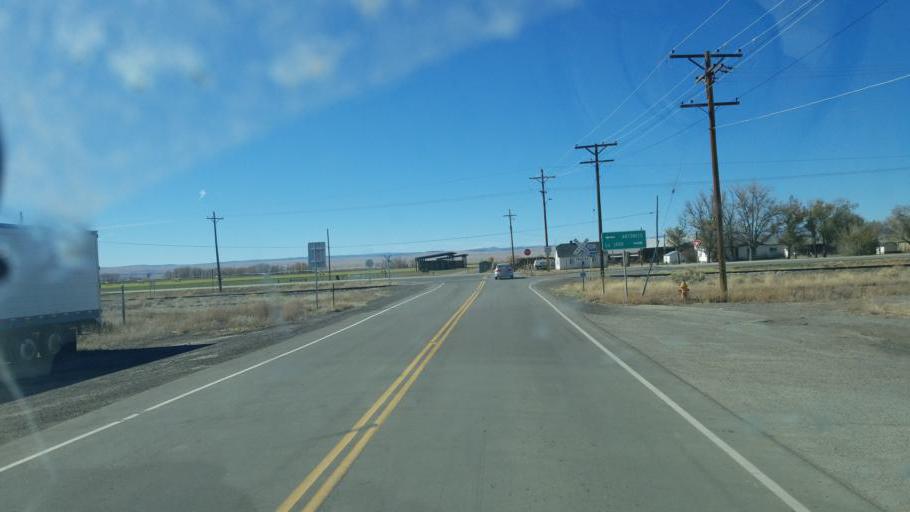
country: US
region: Colorado
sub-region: Conejos County
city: Conejos
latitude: 37.1743
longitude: -105.9868
